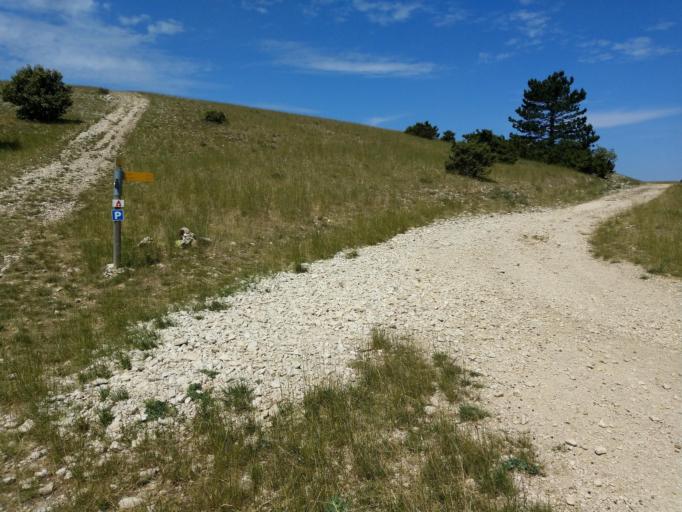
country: FR
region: Provence-Alpes-Cote d'Azur
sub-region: Departement du Vaucluse
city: Cucuron
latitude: 43.8185
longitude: 5.4930
